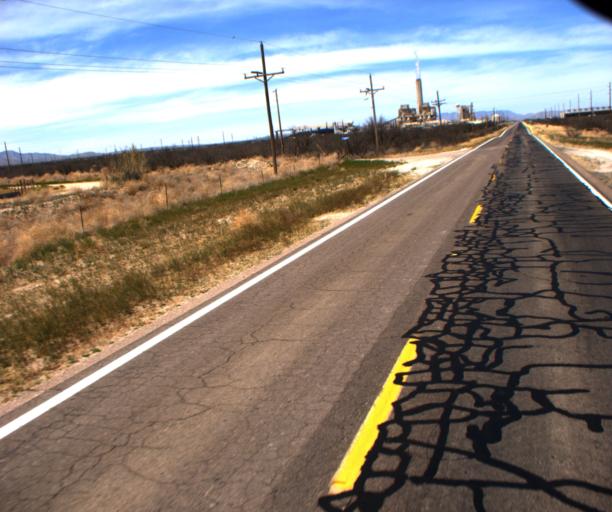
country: US
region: Arizona
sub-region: Cochise County
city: Willcox
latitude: 32.0500
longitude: -109.8860
